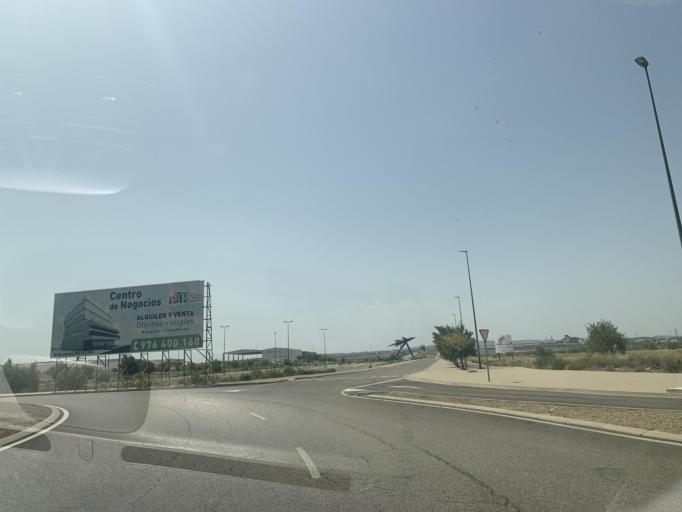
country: ES
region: Aragon
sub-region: Provincia de Zaragoza
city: Zaragoza
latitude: 41.5871
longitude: -0.8385
